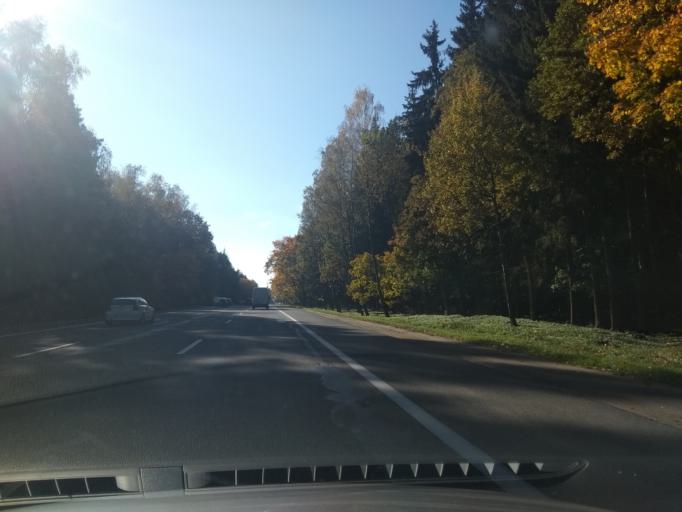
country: BY
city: Fanipol
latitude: 53.7878
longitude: 27.3647
